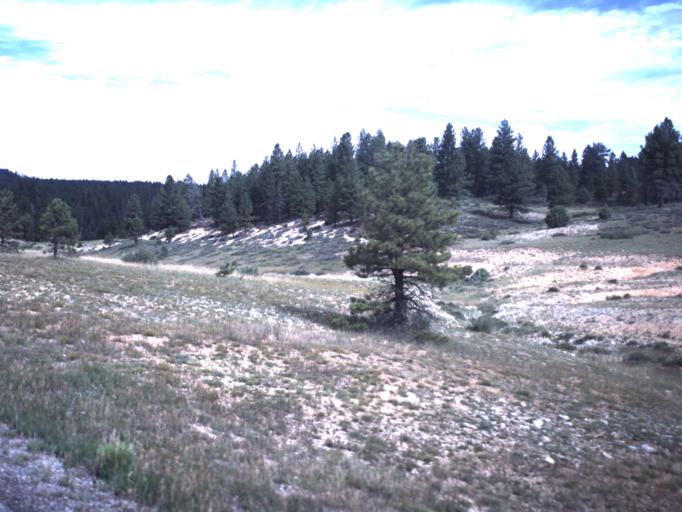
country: US
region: Utah
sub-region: Garfield County
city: Panguitch
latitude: 37.4959
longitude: -112.5823
